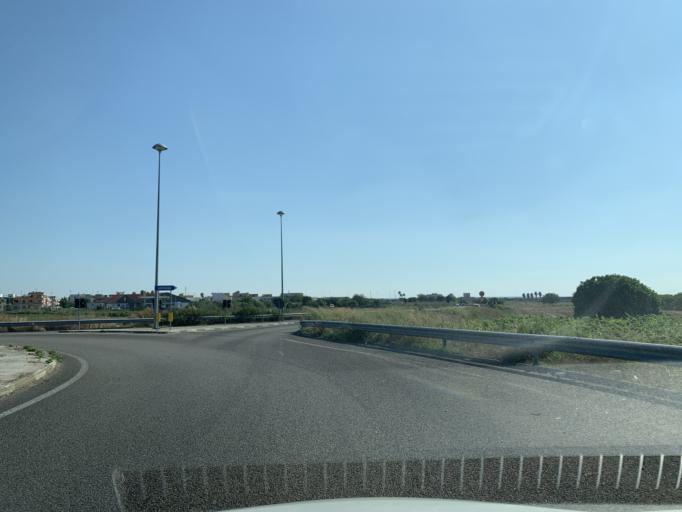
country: IT
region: Apulia
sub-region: Provincia di Lecce
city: Nardo
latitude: 40.1885
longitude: 18.0268
